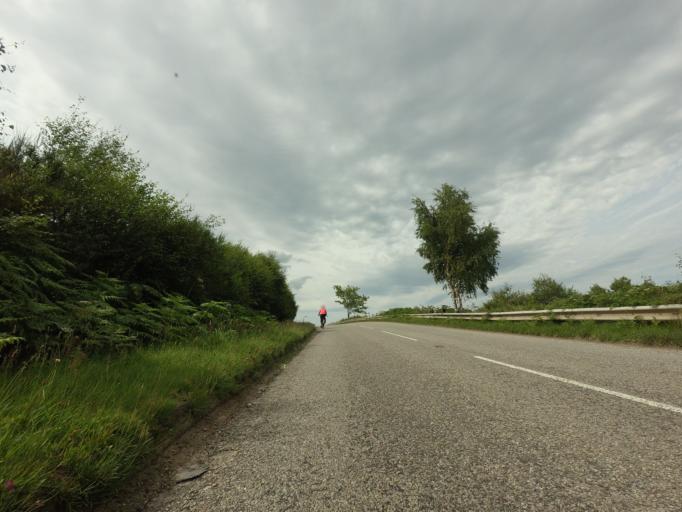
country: GB
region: Scotland
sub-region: Highland
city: Alness
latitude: 57.8623
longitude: -4.3192
